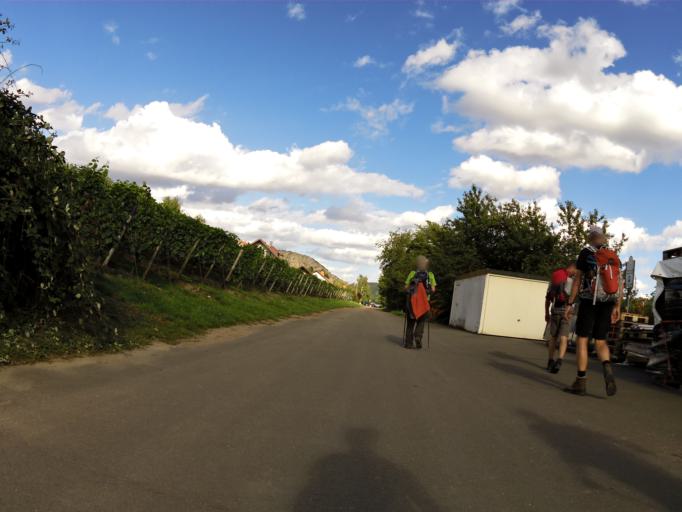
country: DE
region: Rheinland-Pfalz
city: Huffelsheim
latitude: 49.8097
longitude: 7.8078
